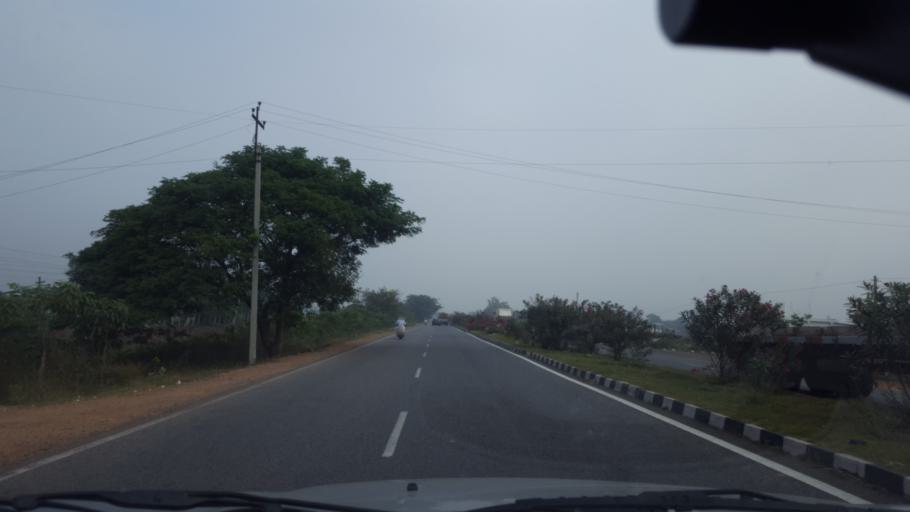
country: IN
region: Andhra Pradesh
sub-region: Guntur
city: Chilakalurupet
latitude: 16.0719
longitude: 80.1541
